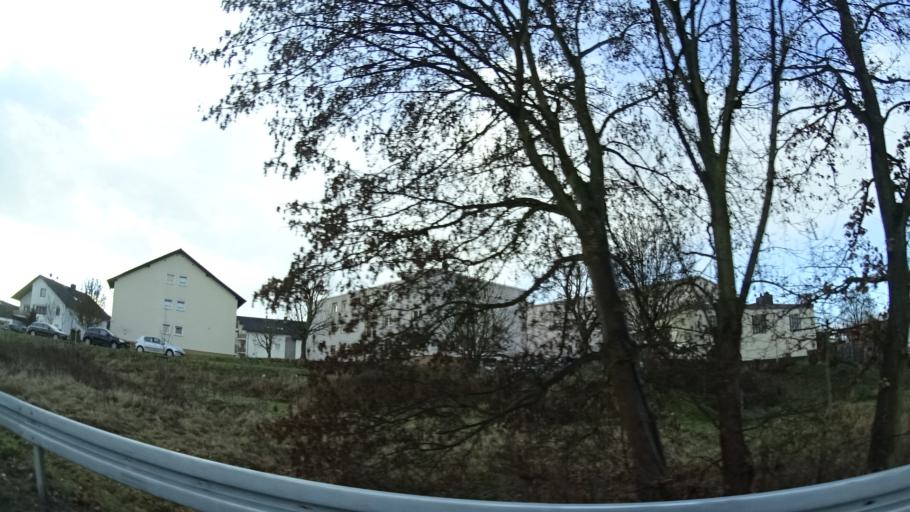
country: DE
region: Hesse
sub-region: Regierungsbezirk Giessen
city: Lich
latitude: 50.5372
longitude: 8.7582
